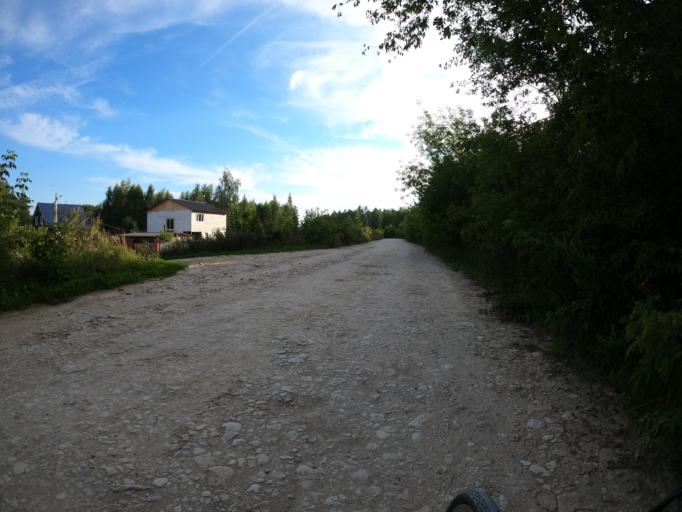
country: RU
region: Moskovskaya
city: Meshcherino
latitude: 55.1382
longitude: 38.3992
